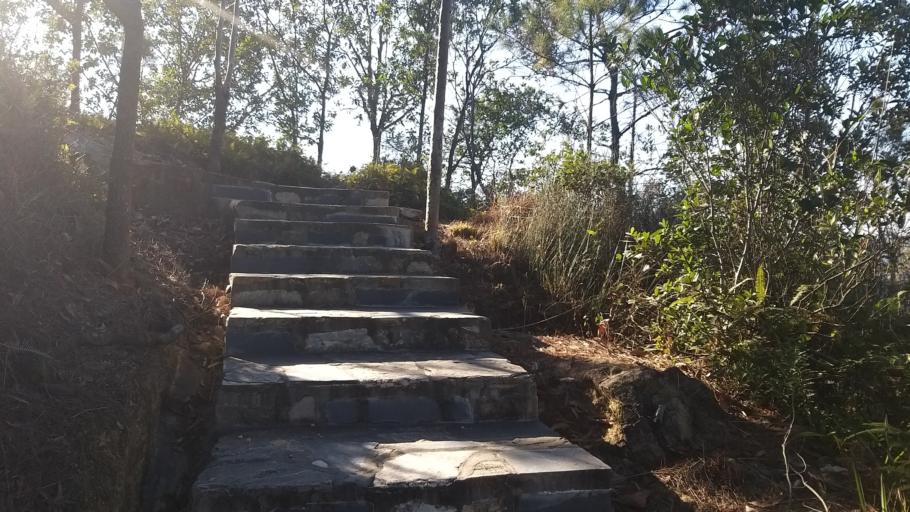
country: HK
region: Tuen Mun
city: Tuen Mun
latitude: 22.4048
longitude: 113.9885
